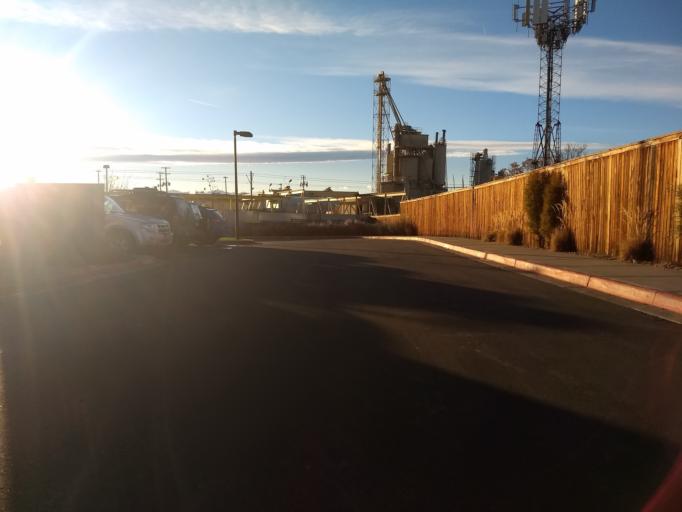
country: US
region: Colorado
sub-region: Denver County
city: Denver
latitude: 39.7131
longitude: -104.9949
